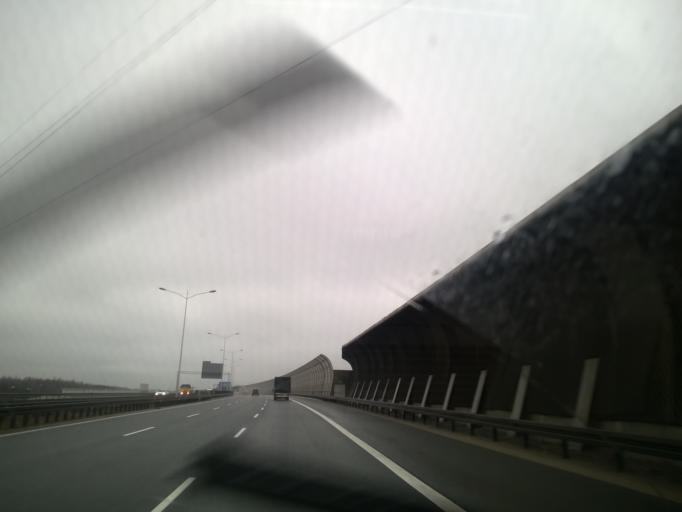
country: PL
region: Lower Silesian Voivodeship
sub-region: Powiat wroclawski
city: Smolec
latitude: 51.1245
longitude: 16.9320
